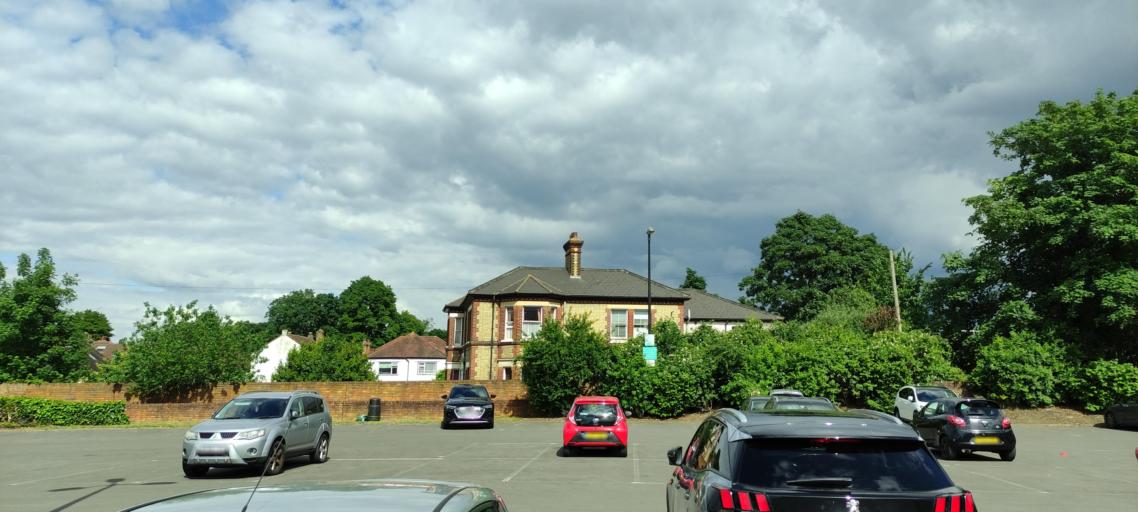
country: GB
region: England
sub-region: Greater London
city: Carshalton
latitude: 51.3683
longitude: -0.1574
